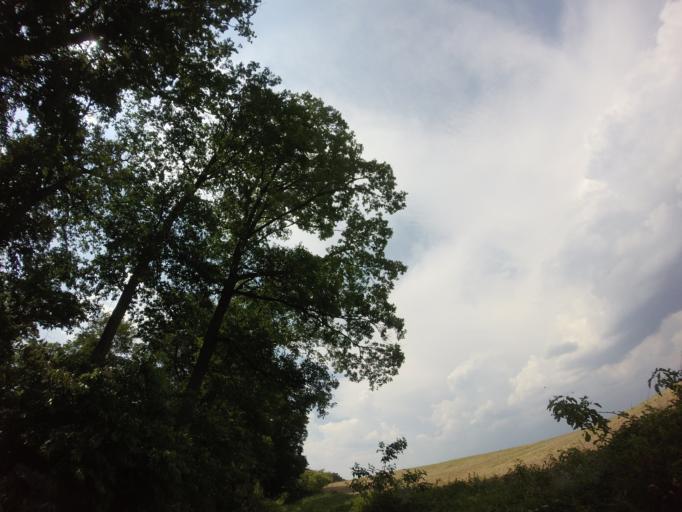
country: PL
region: West Pomeranian Voivodeship
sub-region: Powiat choszczenski
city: Krzecin
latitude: 53.1264
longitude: 15.5941
